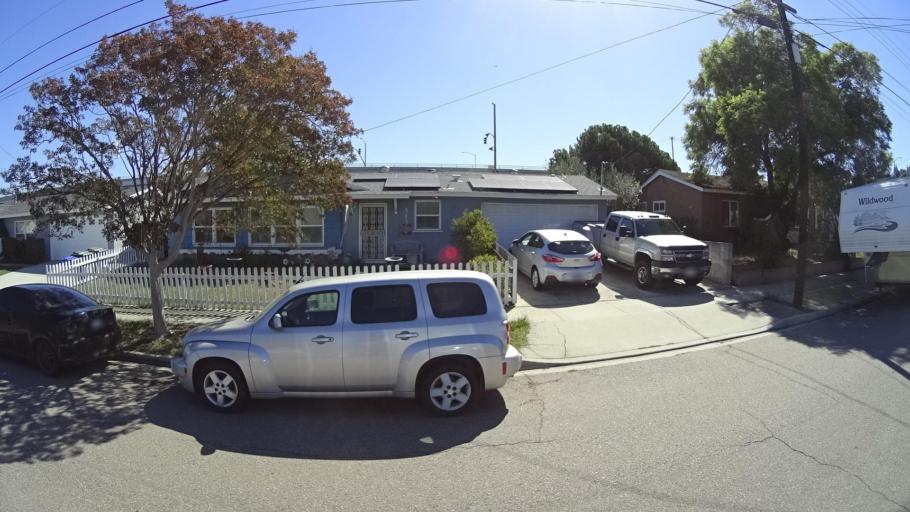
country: US
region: California
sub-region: San Diego County
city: La Presa
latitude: 32.7038
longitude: -117.0125
